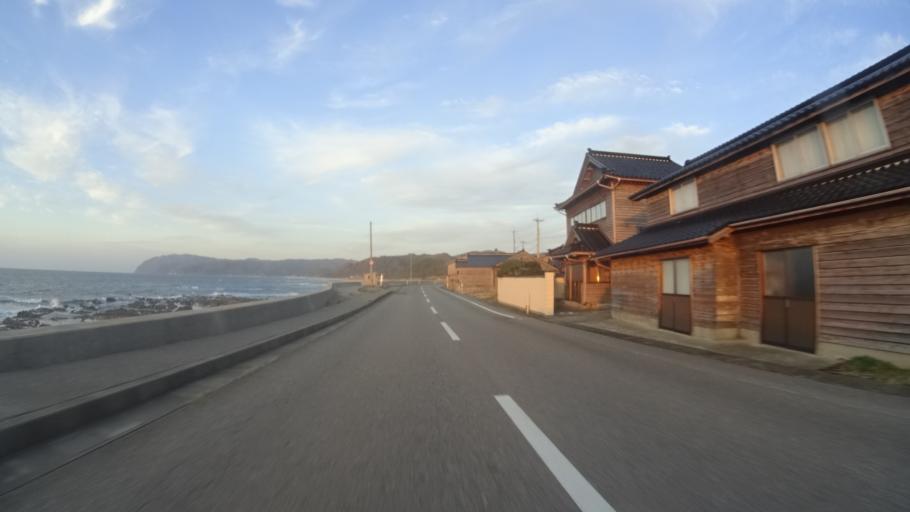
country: JP
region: Ishikawa
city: Nanao
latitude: 37.2541
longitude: 136.7190
